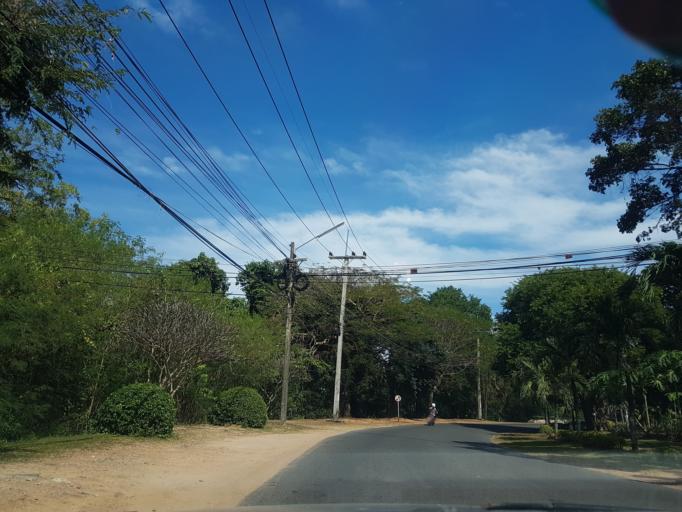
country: TH
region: Chon Buri
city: Sattahip
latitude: 12.6375
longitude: 100.9401
